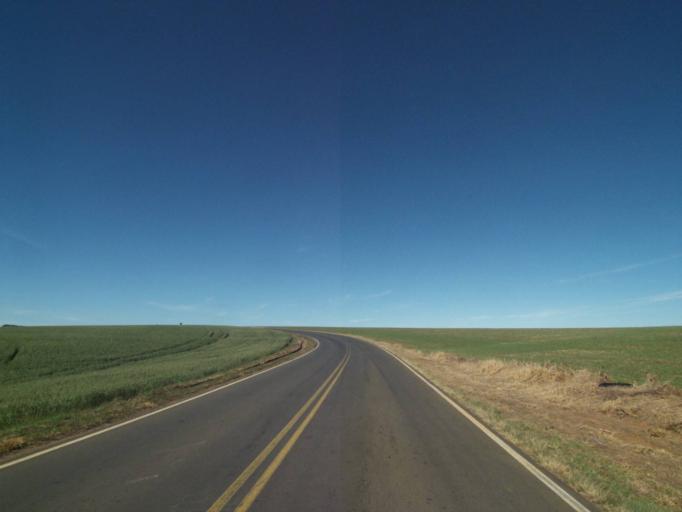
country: BR
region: Parana
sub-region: Tibagi
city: Tibagi
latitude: -24.5627
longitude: -50.2904
